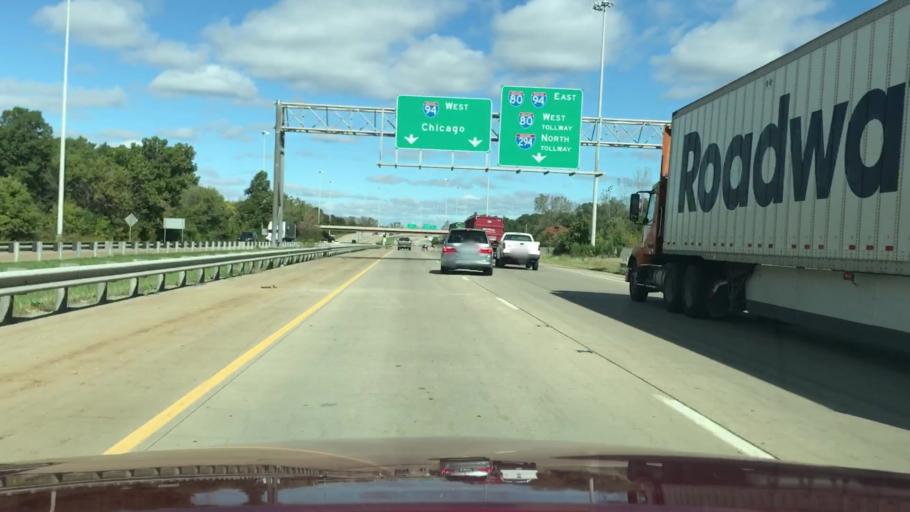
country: US
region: Illinois
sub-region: Cook County
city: Thornton
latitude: 41.5670
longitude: -87.5834
